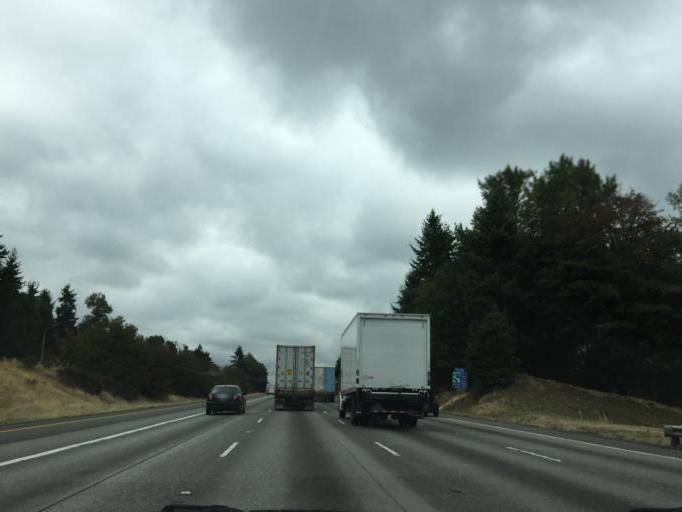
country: US
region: Washington
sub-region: King County
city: Lakeland North
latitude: 47.3648
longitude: -122.2950
